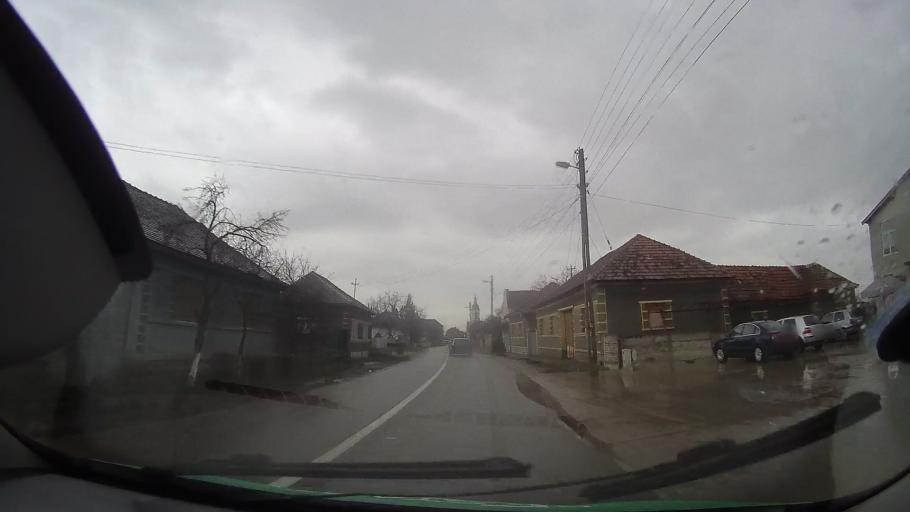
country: RO
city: Capalna
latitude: 46.7153
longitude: 22.0806
